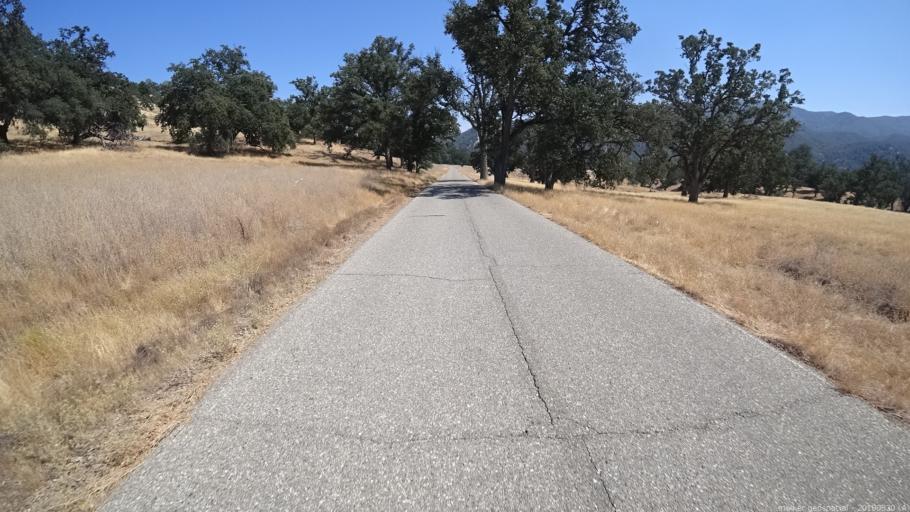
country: US
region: California
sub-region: Monterey County
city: Greenfield
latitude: 36.0781
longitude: -121.3803
